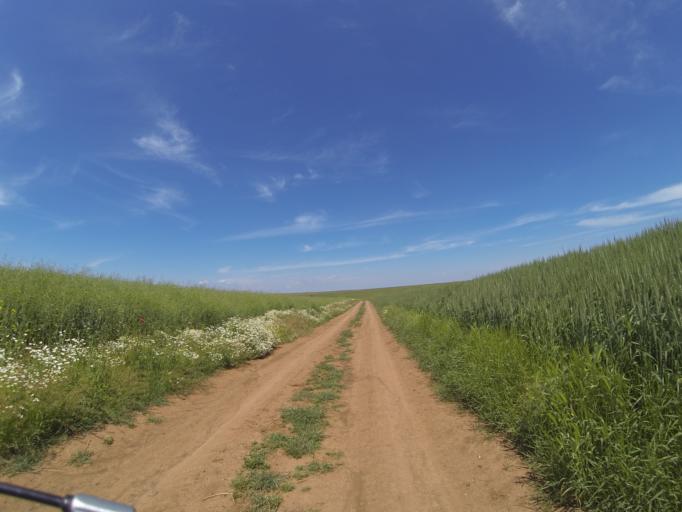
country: RO
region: Dolj
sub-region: Comuna Teslui
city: Teslui
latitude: 44.1753
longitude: 24.1673
